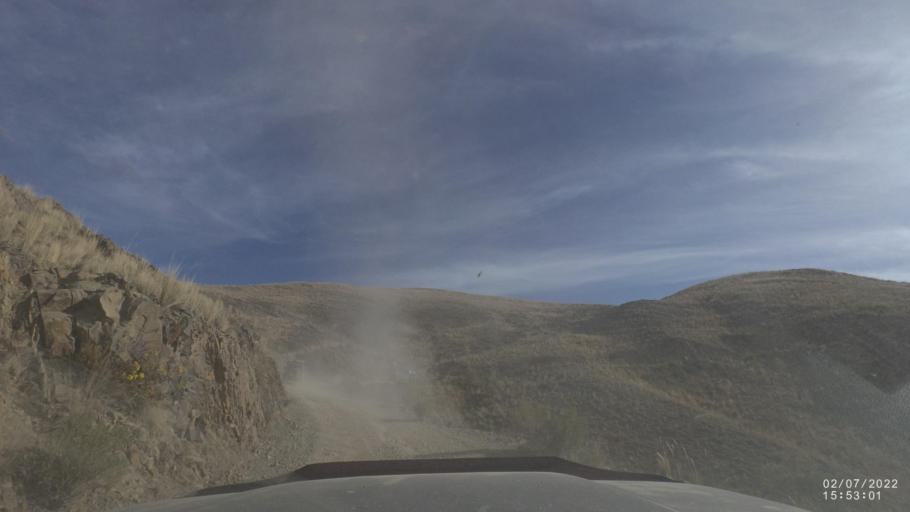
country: BO
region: Cochabamba
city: Irpa Irpa
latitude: -17.9086
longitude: -66.4154
